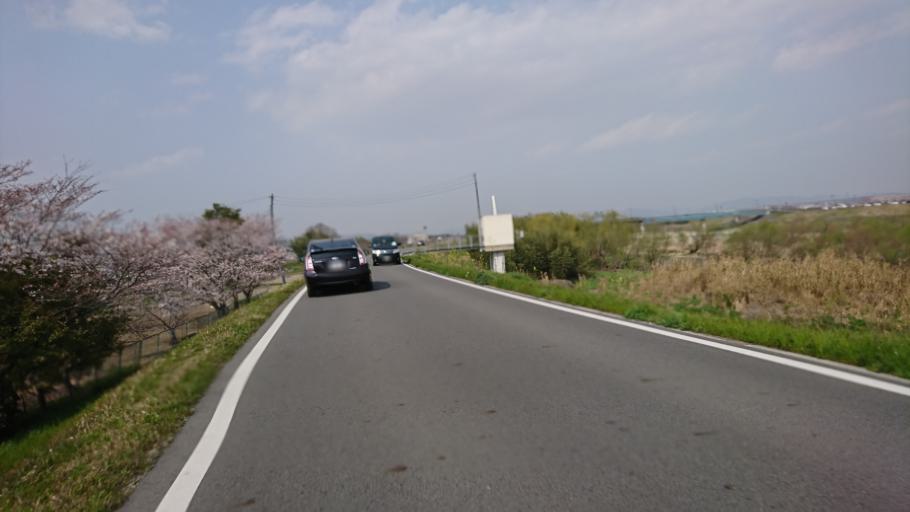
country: JP
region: Hyogo
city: Ono
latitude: 34.8739
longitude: 134.9234
